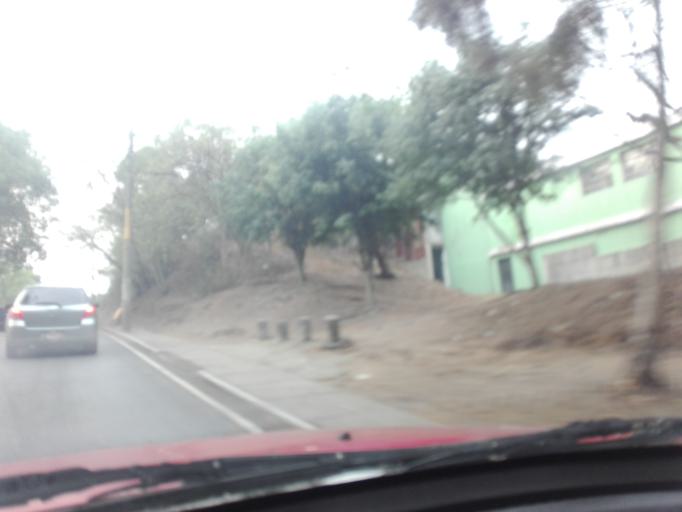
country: GT
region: Guatemala
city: Guatemala City
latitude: 14.6426
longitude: -90.5509
